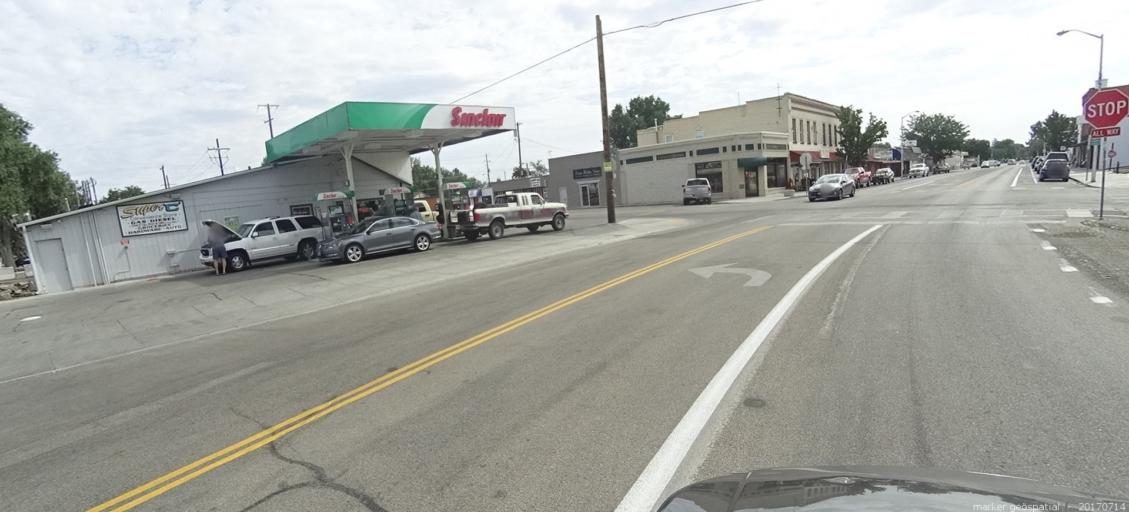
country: US
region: Idaho
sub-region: Ada County
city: Kuna
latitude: 43.4907
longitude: -116.4198
